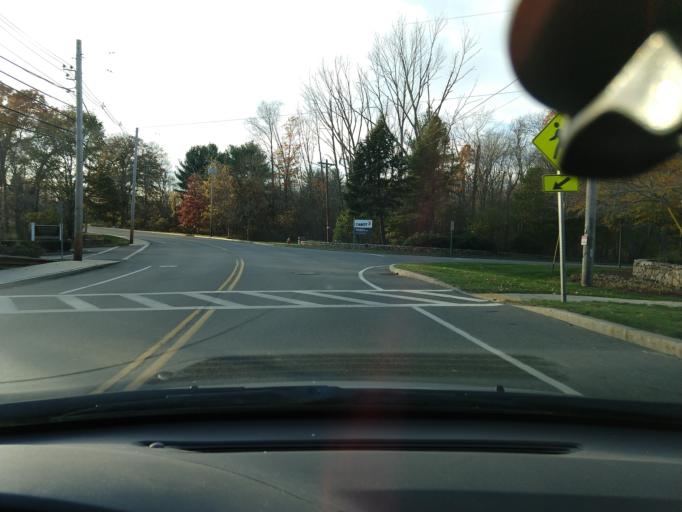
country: US
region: Massachusetts
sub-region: Middlesex County
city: Billerica
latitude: 42.5492
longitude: -71.2775
